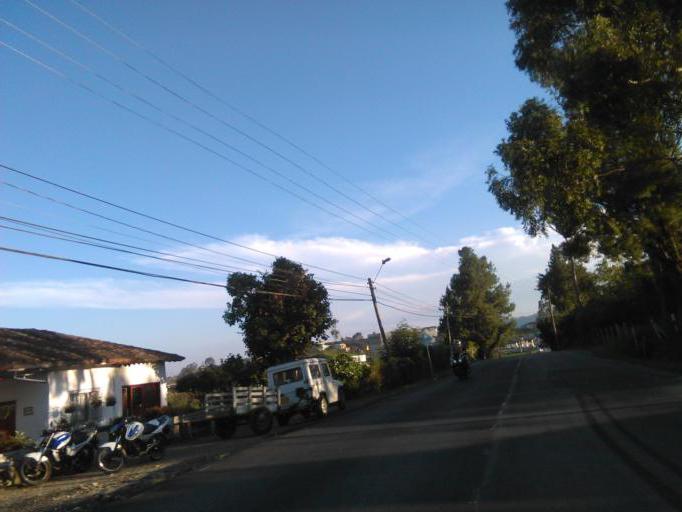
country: CO
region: Antioquia
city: La Union
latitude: 5.9859
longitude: -75.3717
